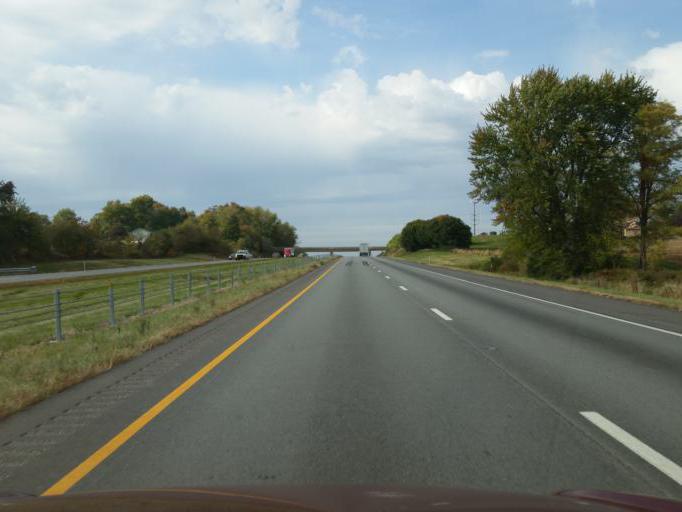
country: US
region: Pennsylvania
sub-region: Lancaster County
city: Rheems
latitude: 40.1528
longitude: -76.5680
